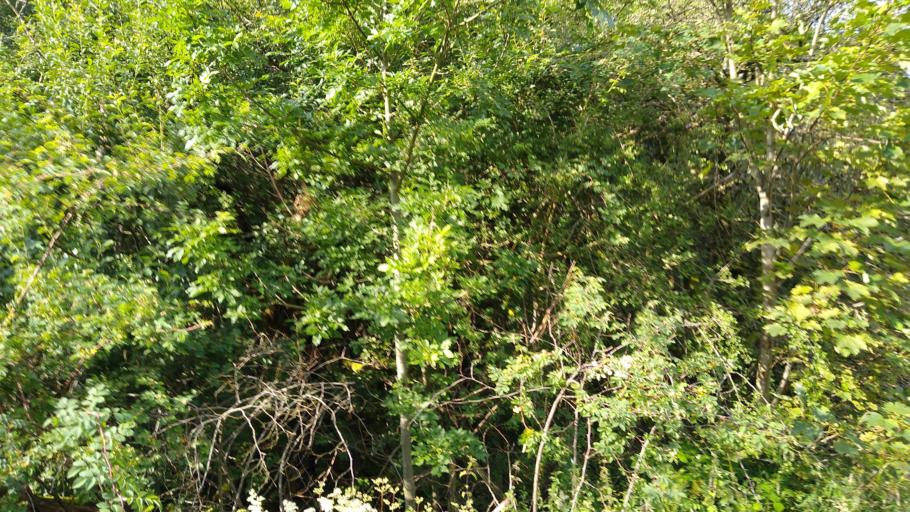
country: GB
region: England
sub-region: Cumbria
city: Keswick
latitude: 54.6150
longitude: -3.0423
